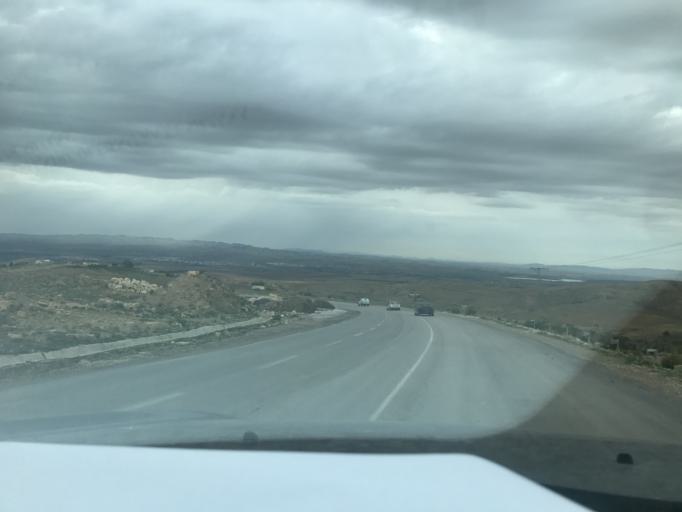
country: TN
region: Silyanah
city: Siliana
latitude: 36.0920
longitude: 9.4728
